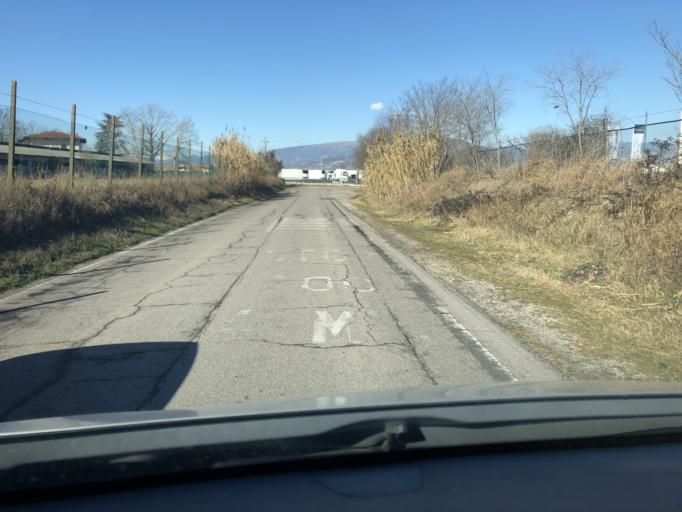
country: IT
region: Veneto
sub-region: Provincia di Verona
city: Bassone
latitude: 45.4521
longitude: 10.8800
